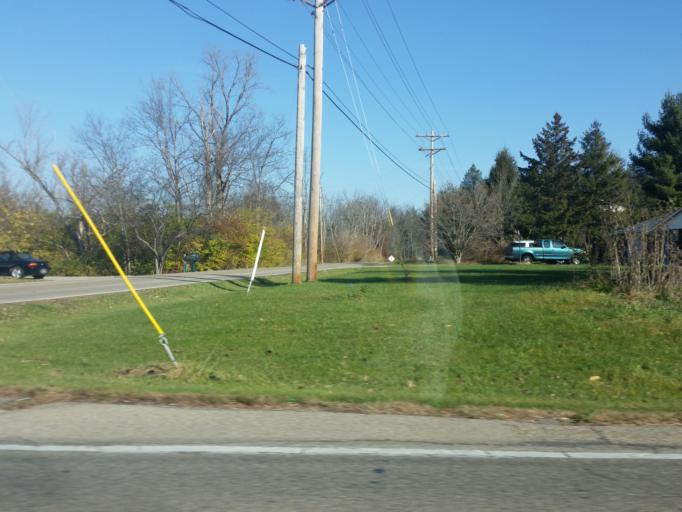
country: US
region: Ohio
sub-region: Butler County
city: Oxford
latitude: 39.4718
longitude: -84.7050
